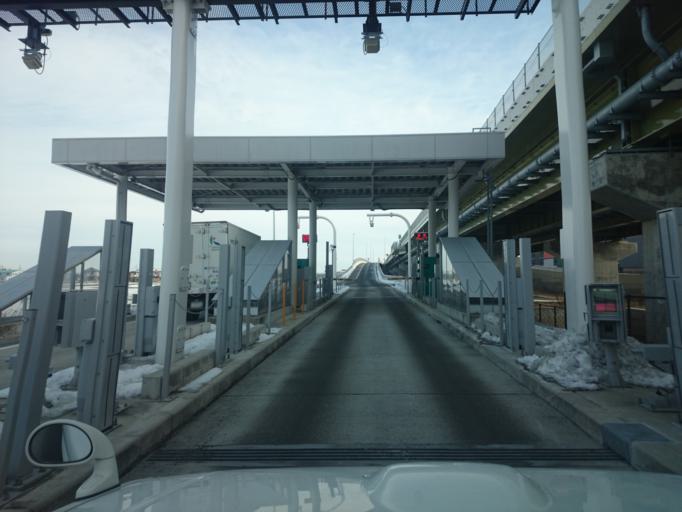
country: JP
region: Saitama
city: Satte
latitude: 36.0669
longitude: 139.7426
